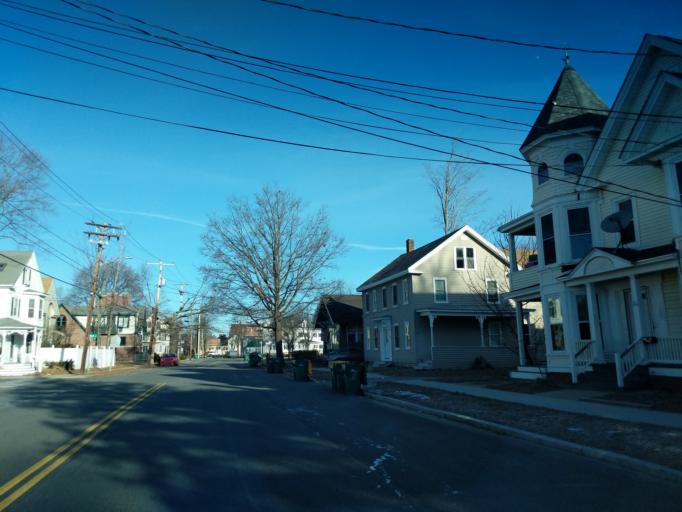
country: US
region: New Hampshire
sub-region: Strafford County
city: Rochester
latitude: 43.3011
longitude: -70.9757
